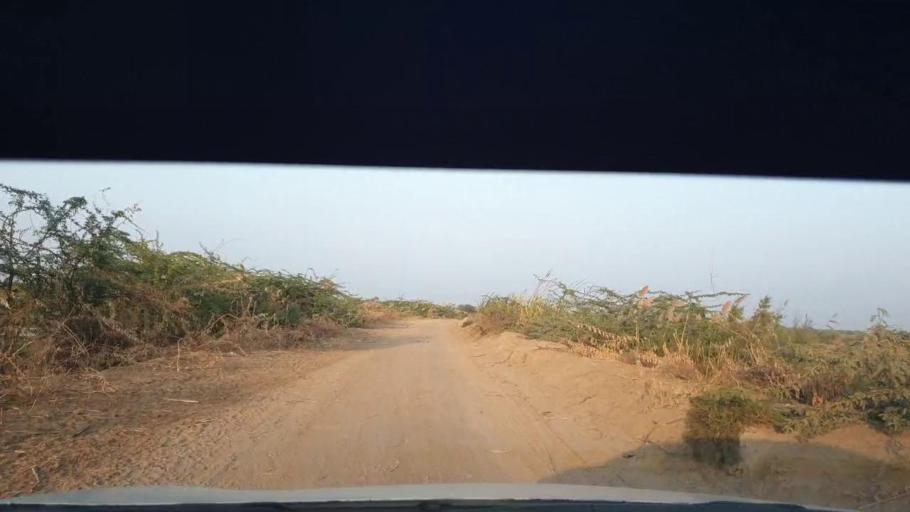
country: PK
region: Sindh
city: Berani
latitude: 25.7473
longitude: 68.9744
